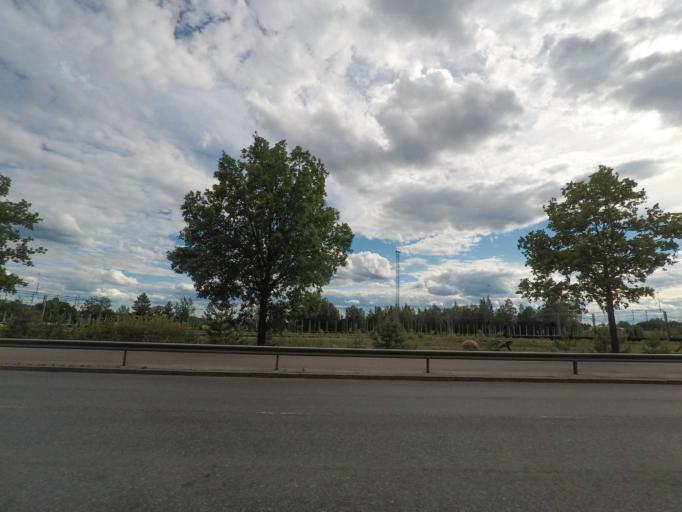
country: FI
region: Paijanne Tavastia
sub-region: Lahti
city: Lahti
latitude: 60.9778
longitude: 25.6467
